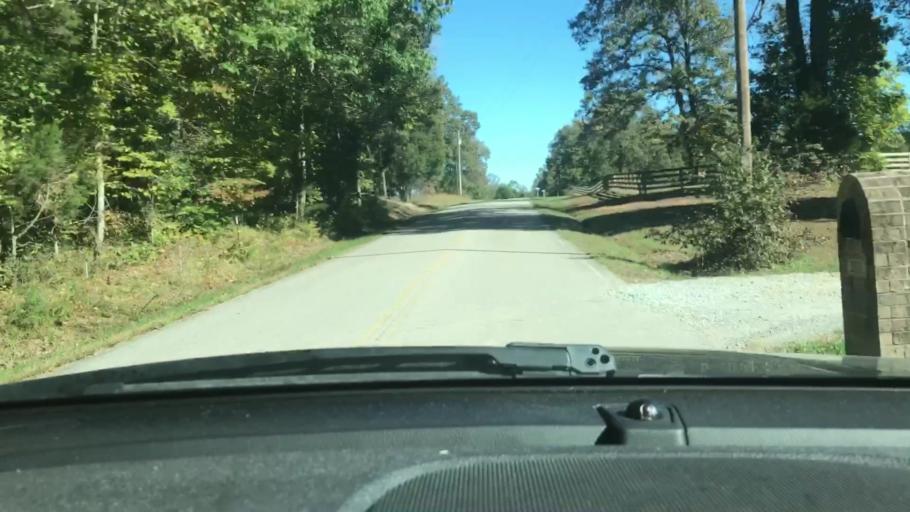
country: US
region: Tennessee
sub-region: Dickson County
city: Charlotte
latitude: 36.1804
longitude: -87.2958
